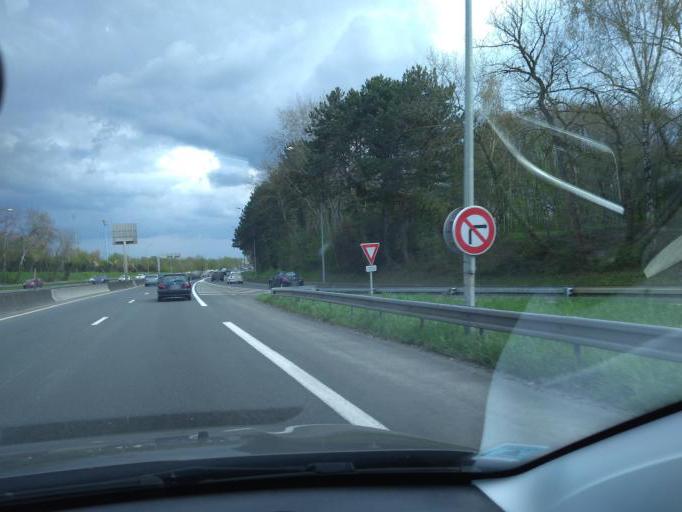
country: FR
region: Pays de la Loire
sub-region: Departement de Maine-et-Loire
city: Avrille
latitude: 47.4689
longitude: -0.5881
